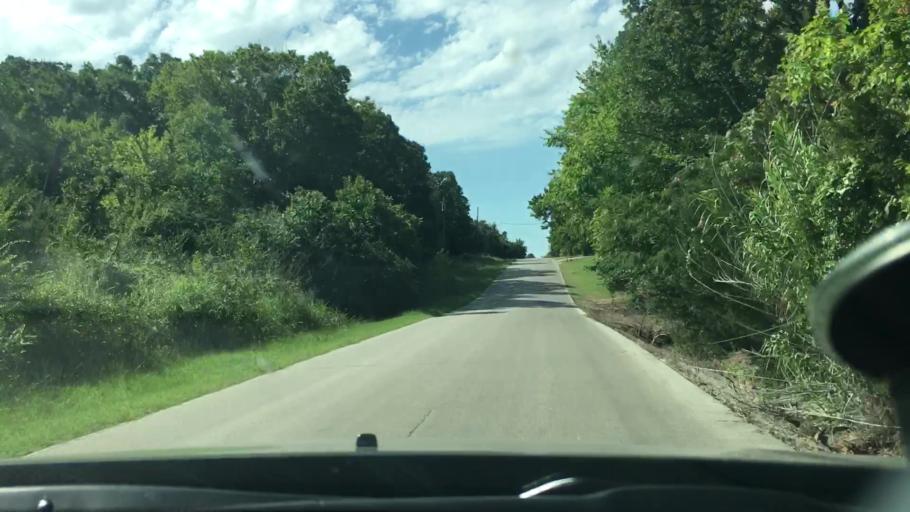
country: US
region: Oklahoma
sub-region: Carter County
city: Ardmore
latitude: 34.1498
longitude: -97.0906
